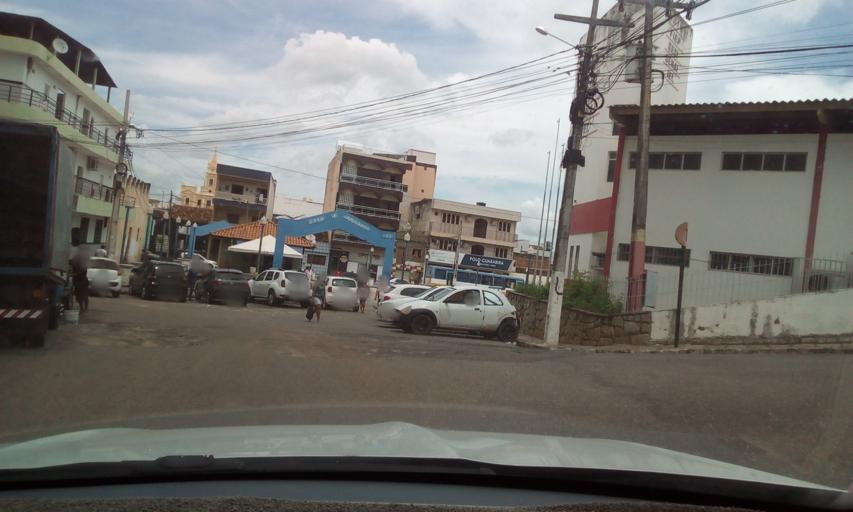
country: BR
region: Paraiba
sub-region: Guarabira
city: Guarabira
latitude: -6.8536
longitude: -35.4908
